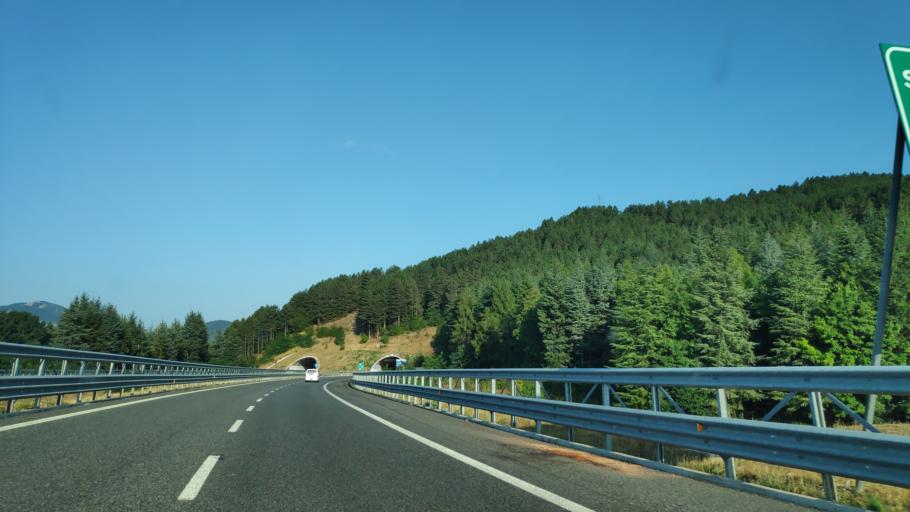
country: IT
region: Calabria
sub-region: Provincia di Cosenza
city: Morano Calabro
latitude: 39.8641
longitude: 16.0863
